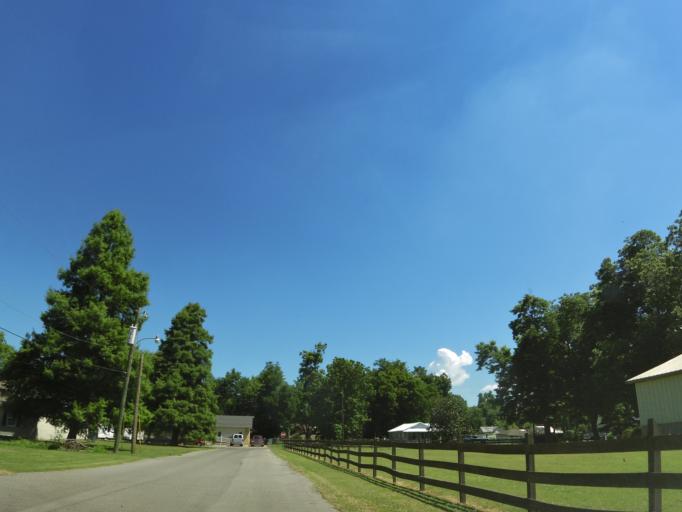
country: US
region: Missouri
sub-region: New Madrid County
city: New Madrid
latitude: 36.5853
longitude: -89.5340
